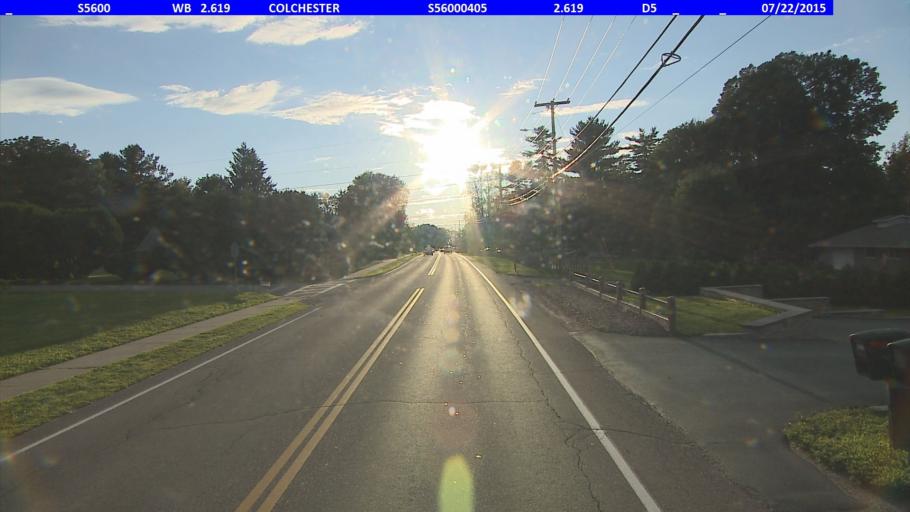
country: US
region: Vermont
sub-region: Chittenden County
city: Winooski
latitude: 44.5497
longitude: -73.2254
